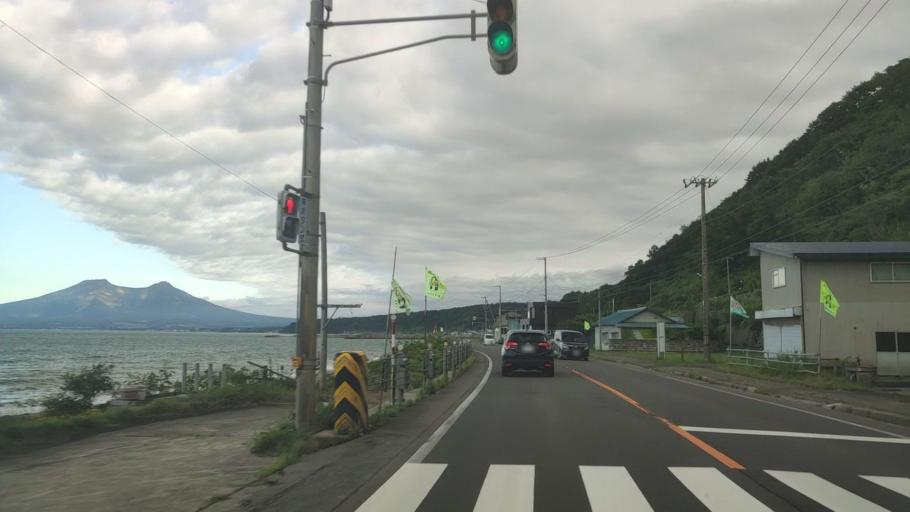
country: JP
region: Hokkaido
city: Nanae
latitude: 42.1416
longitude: 140.5026
